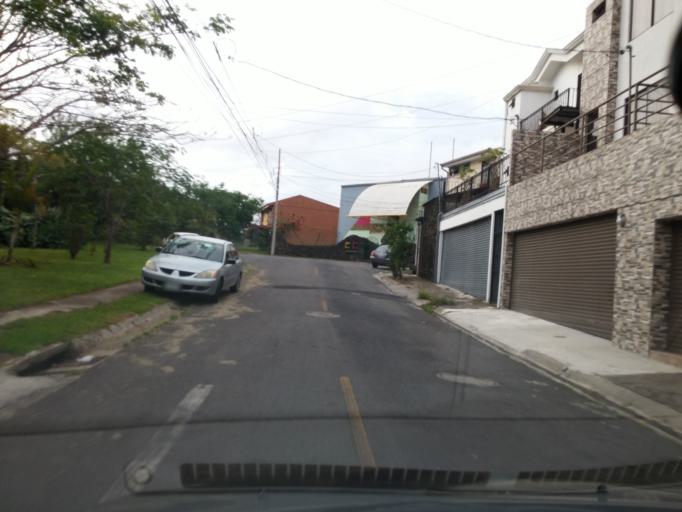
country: CR
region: Heredia
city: Heredia
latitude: 10.0163
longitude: -84.1217
